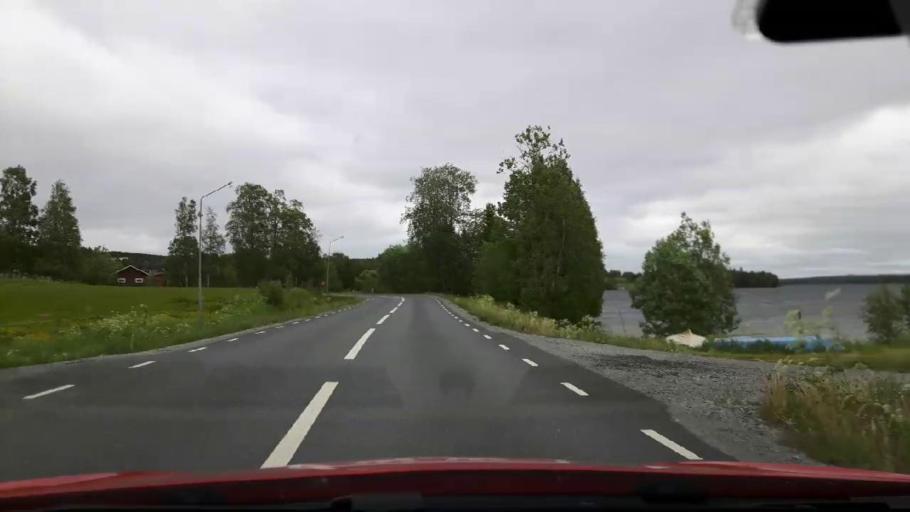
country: SE
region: Jaemtland
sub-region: OEstersunds Kommun
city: Lit
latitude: 63.7430
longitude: 14.8348
